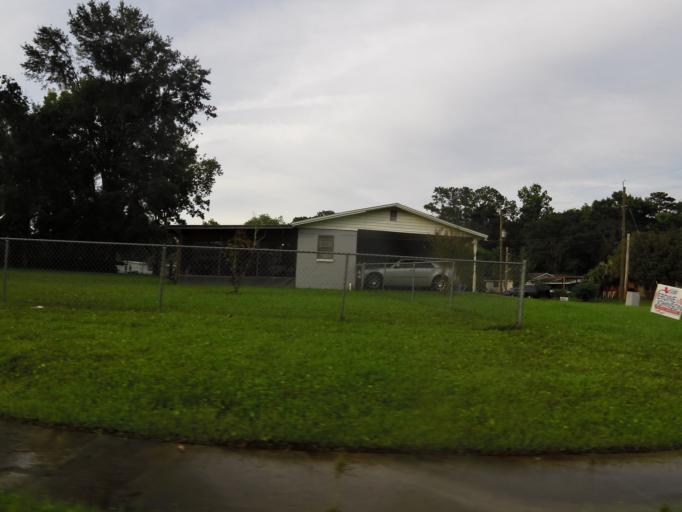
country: US
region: Florida
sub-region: Duval County
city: Jacksonville
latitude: 30.3989
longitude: -81.7193
